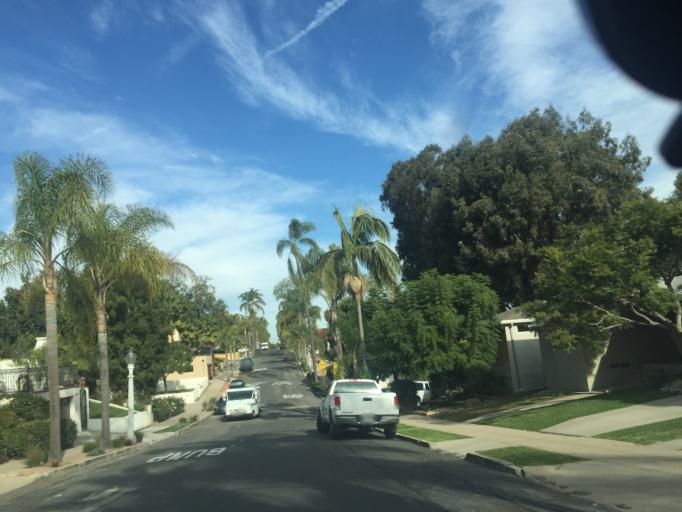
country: US
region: California
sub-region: San Diego County
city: San Diego
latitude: 32.7598
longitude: -117.1024
